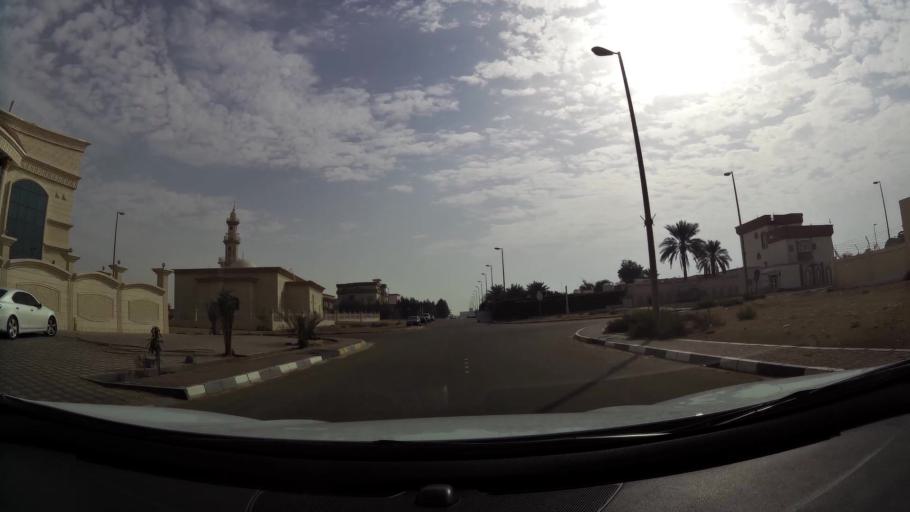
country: AE
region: Abu Dhabi
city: Abu Dhabi
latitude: 24.2578
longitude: 54.7066
